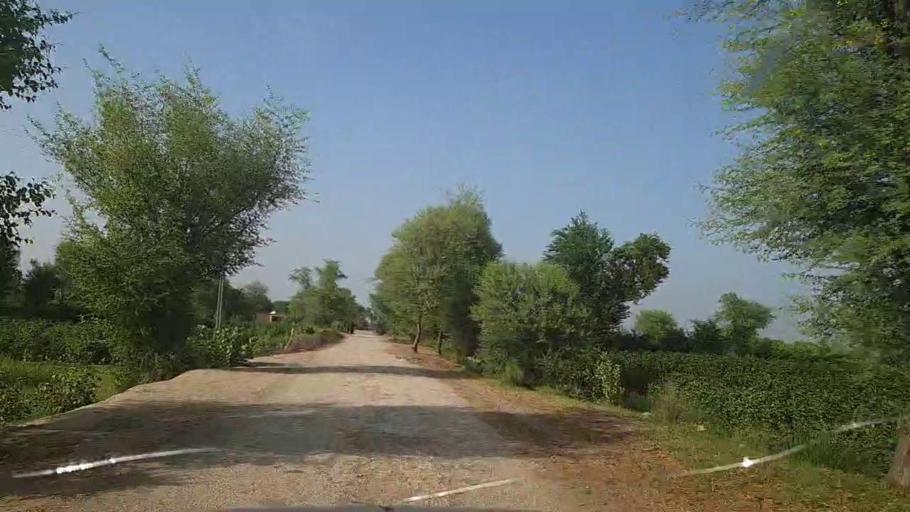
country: PK
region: Sindh
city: Khanpur
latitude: 27.7273
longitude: 69.3313
